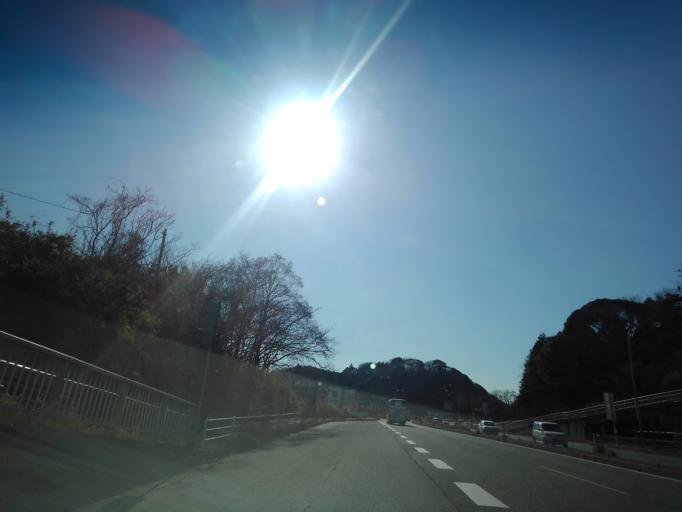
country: JP
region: Chiba
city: Kisarazu
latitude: 35.3487
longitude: 139.9208
